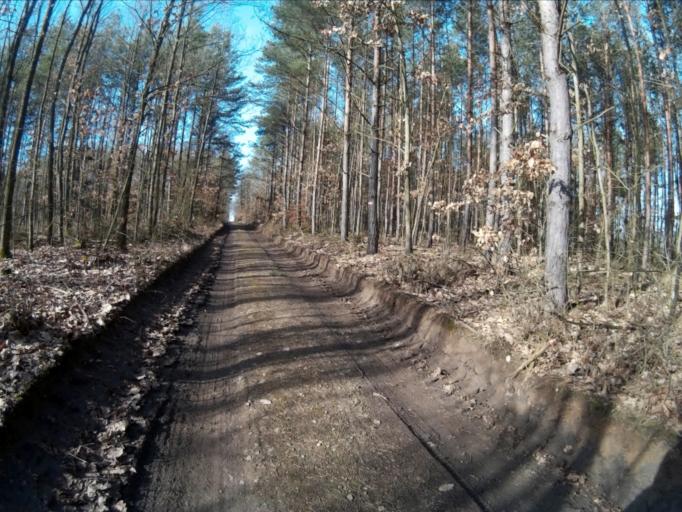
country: CZ
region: Vysocina
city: Mohelno
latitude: 49.1408
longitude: 16.1964
